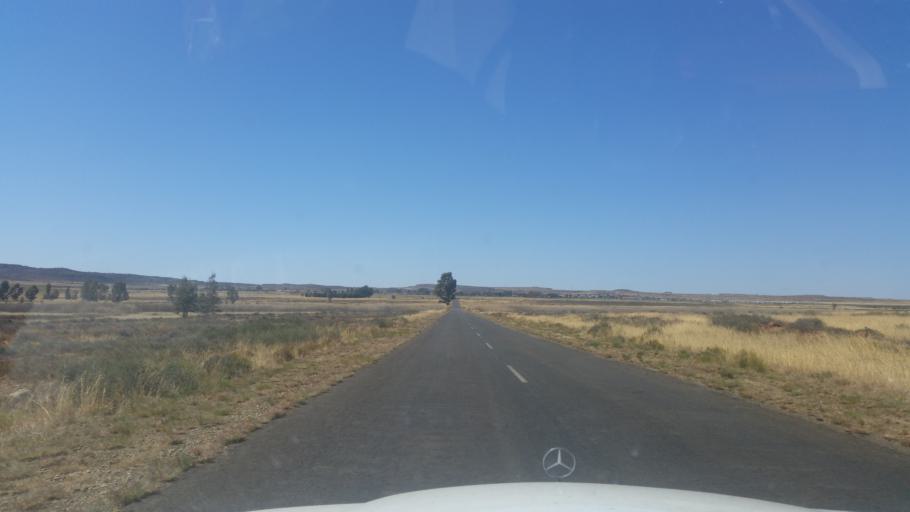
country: ZA
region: Eastern Cape
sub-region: Joe Gqabi District Municipality
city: Burgersdorp
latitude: -30.7556
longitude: 25.7745
